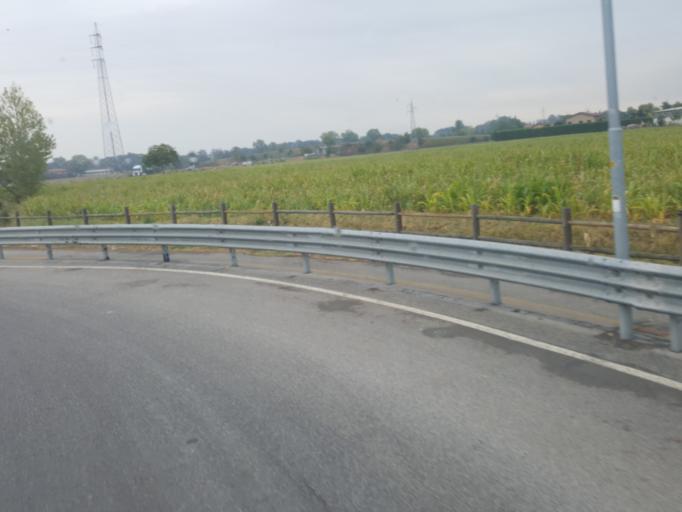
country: IT
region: Emilia-Romagna
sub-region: Provincia di Modena
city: Fiorano
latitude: 44.5496
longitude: 10.8211
